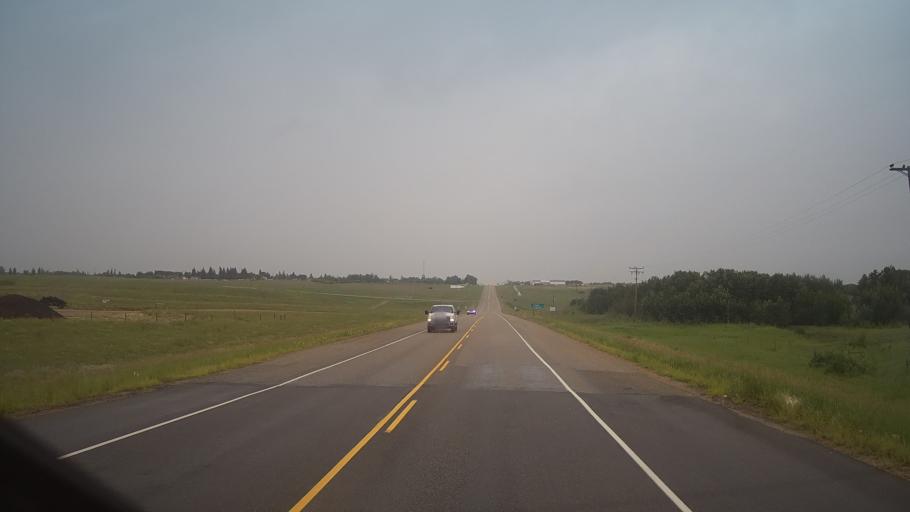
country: CA
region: Saskatchewan
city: Biggar
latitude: 52.0578
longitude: -107.9566
